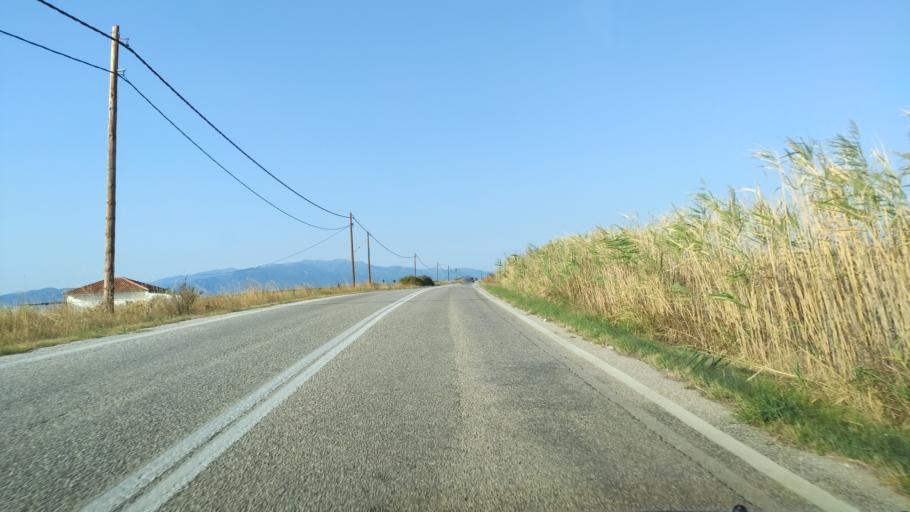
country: GR
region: East Macedonia and Thrace
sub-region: Nomos Rodopis
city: Iasmos
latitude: 40.9890
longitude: 25.1618
